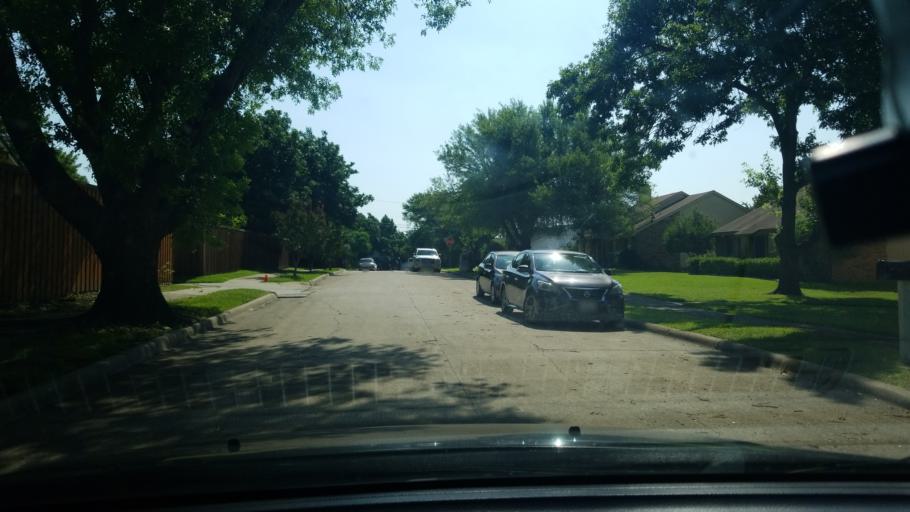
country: US
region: Texas
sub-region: Dallas County
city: Mesquite
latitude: 32.8184
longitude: -96.6238
